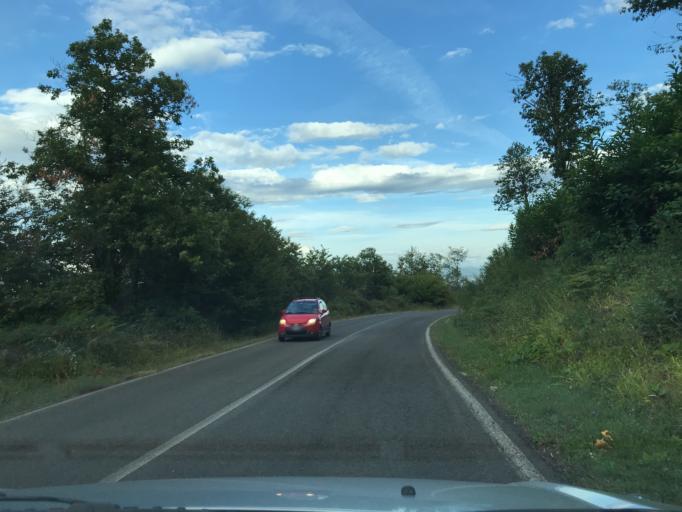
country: IT
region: Umbria
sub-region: Provincia di Terni
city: Guardea
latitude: 42.6524
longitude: 12.3506
